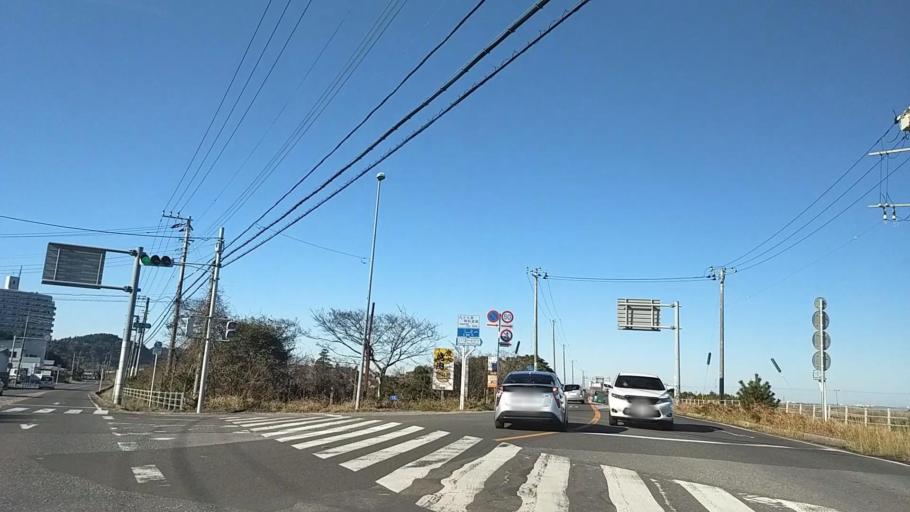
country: JP
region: Chiba
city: Ohara
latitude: 35.3331
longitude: 140.3926
